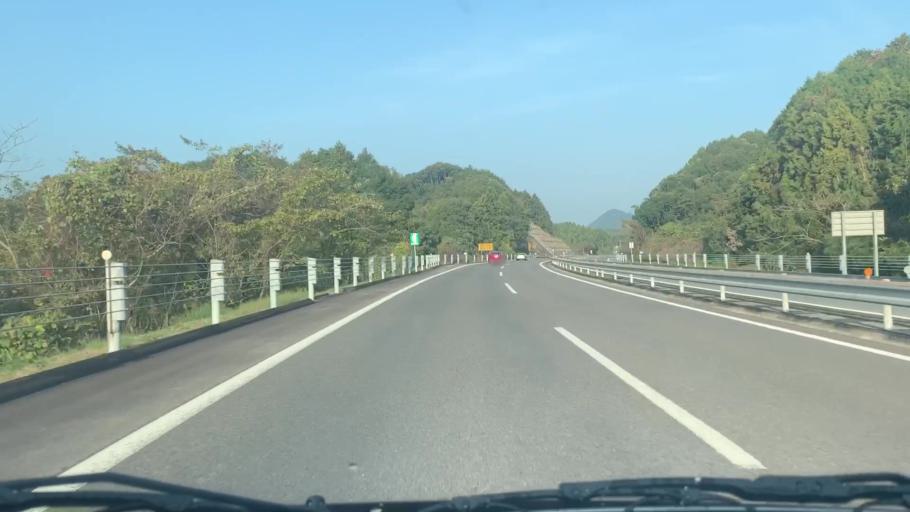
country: JP
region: Saga Prefecture
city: Ureshinomachi-shimojuku
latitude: 33.1497
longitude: 129.9371
